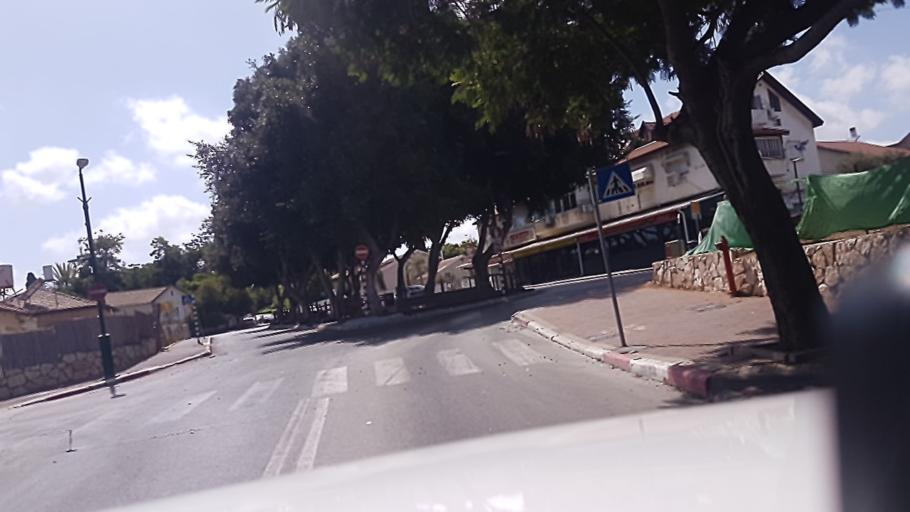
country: IL
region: Central District
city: Ganne Tiqwa
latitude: 32.0636
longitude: 34.8582
